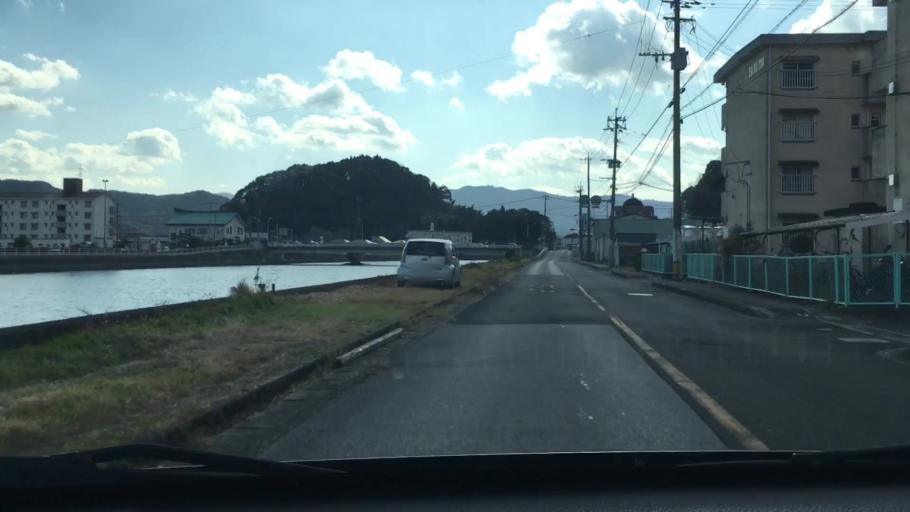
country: JP
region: Oita
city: Saiki
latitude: 32.9637
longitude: 131.9128
